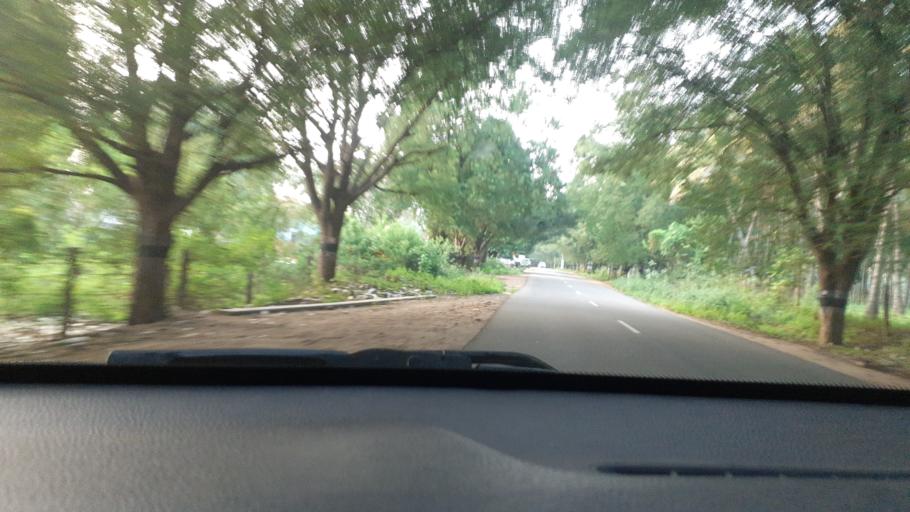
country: IN
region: Tamil Nadu
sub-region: Dindigul
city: Palani
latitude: 10.4267
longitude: 77.5321
